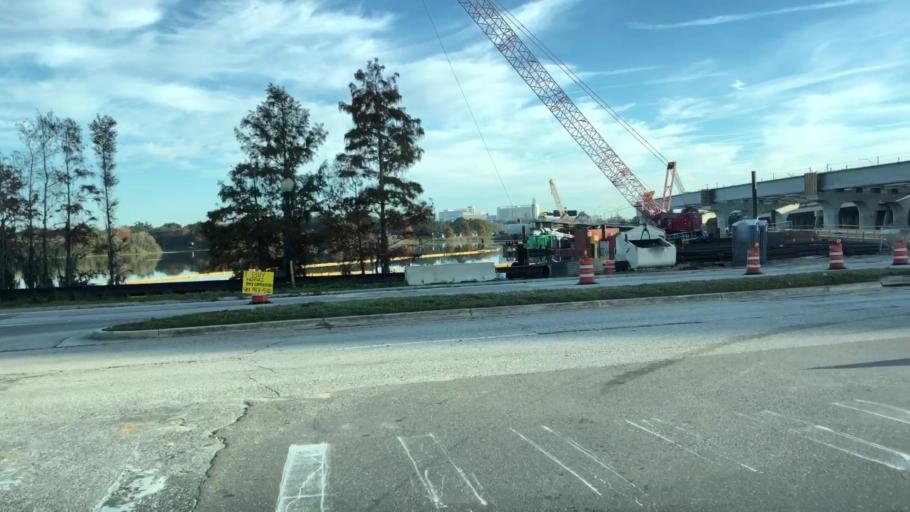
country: US
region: Florida
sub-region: Orange County
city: Orlando
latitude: 28.5599
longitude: -81.3814
